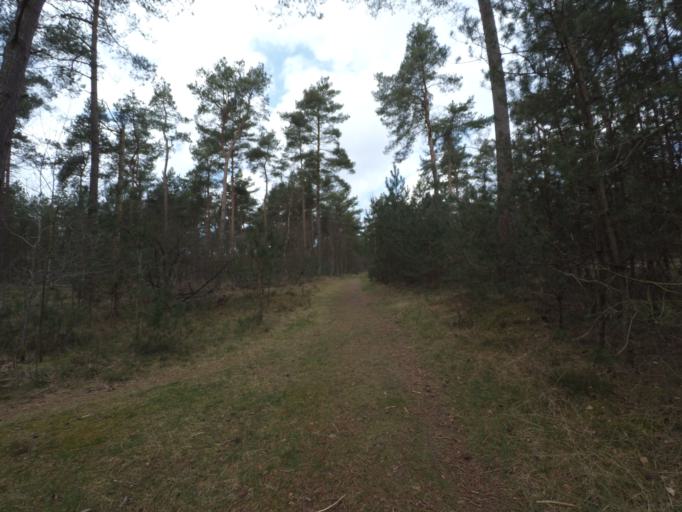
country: NL
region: Utrecht
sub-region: Gemeente Amersfoort
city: Amersfoort
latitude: 52.1234
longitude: 5.3702
